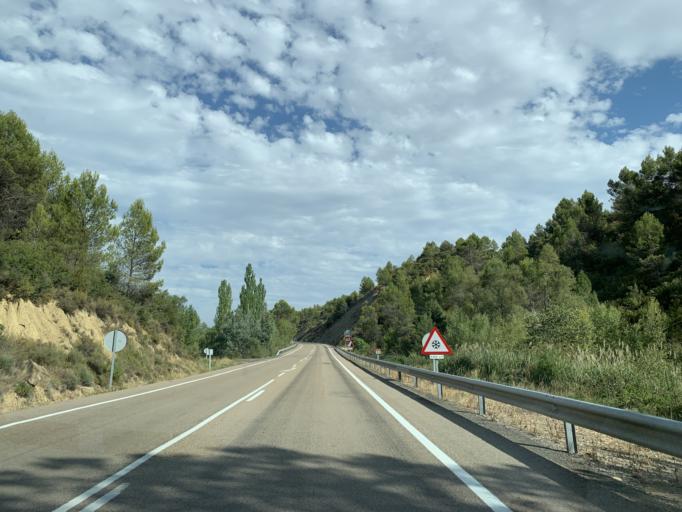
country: ES
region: Aragon
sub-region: Provincia de Zaragoza
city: Santa Eulalia de Gallego
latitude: 42.2947
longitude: -0.7292
